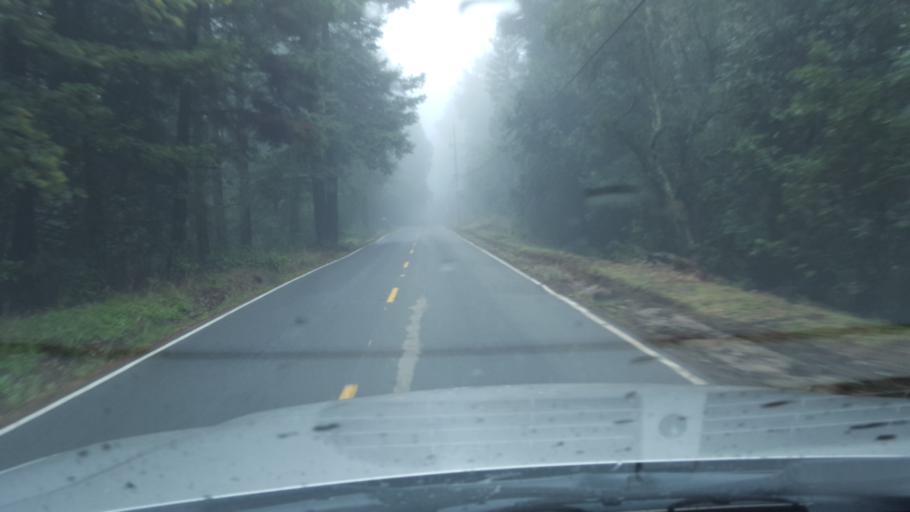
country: US
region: California
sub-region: Santa Cruz County
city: Interlaken
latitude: 37.0265
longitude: -121.7375
